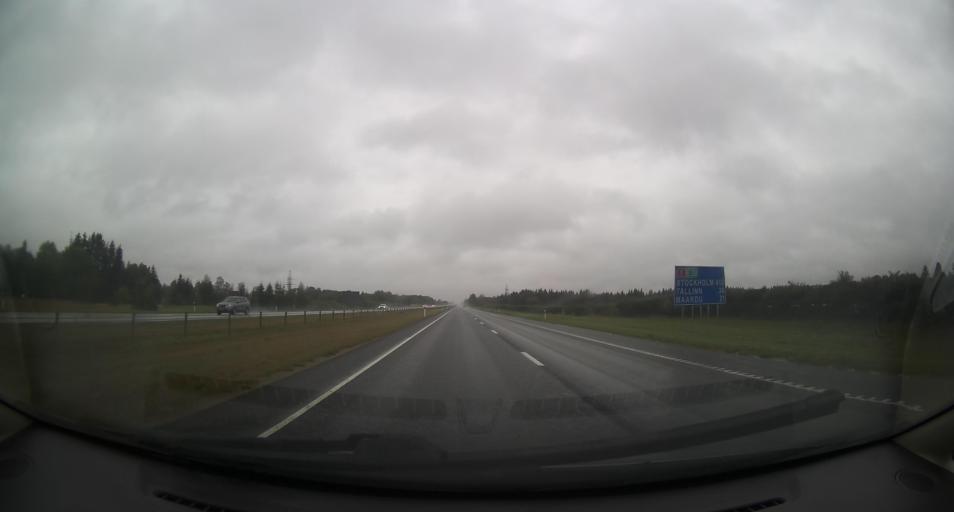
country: EE
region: Harju
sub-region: Kuusalu vald
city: Kuusalu
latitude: 59.4451
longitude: 25.3657
